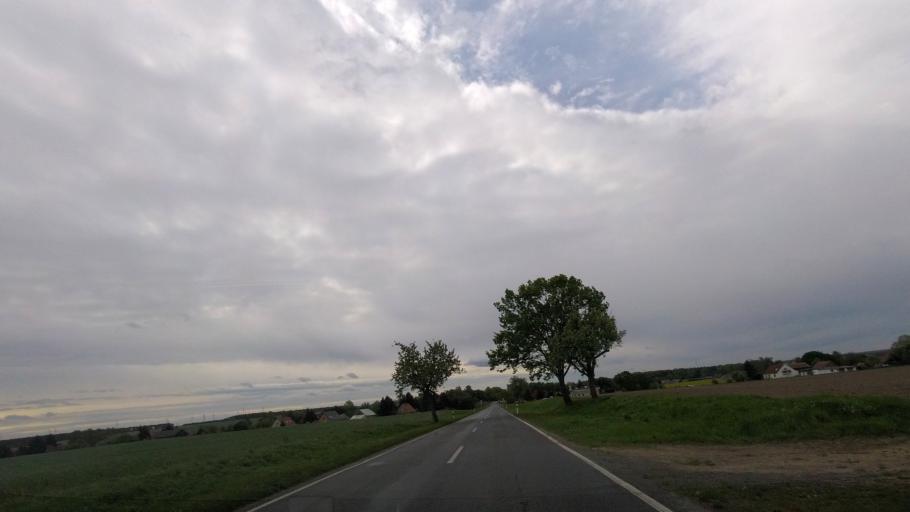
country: DE
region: Brandenburg
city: Dahme
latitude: 51.9072
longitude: 13.4048
